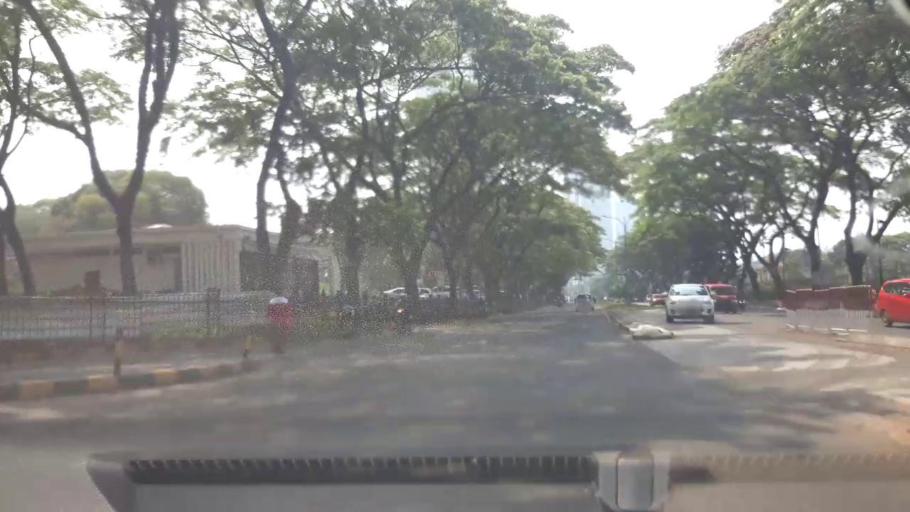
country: ID
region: Banten
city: Tangerang
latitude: -6.2261
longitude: 106.5983
